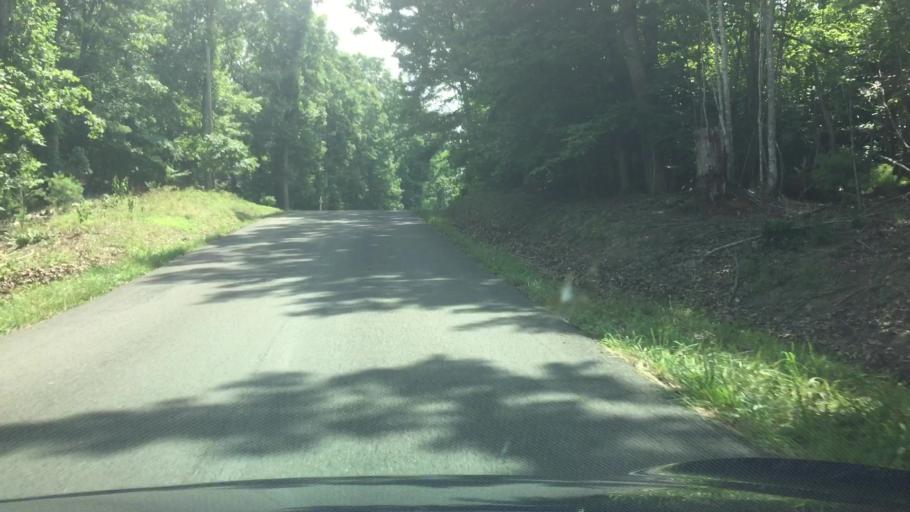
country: US
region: Virginia
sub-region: Wythe County
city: Wytheville
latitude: 36.9243
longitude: -81.0315
